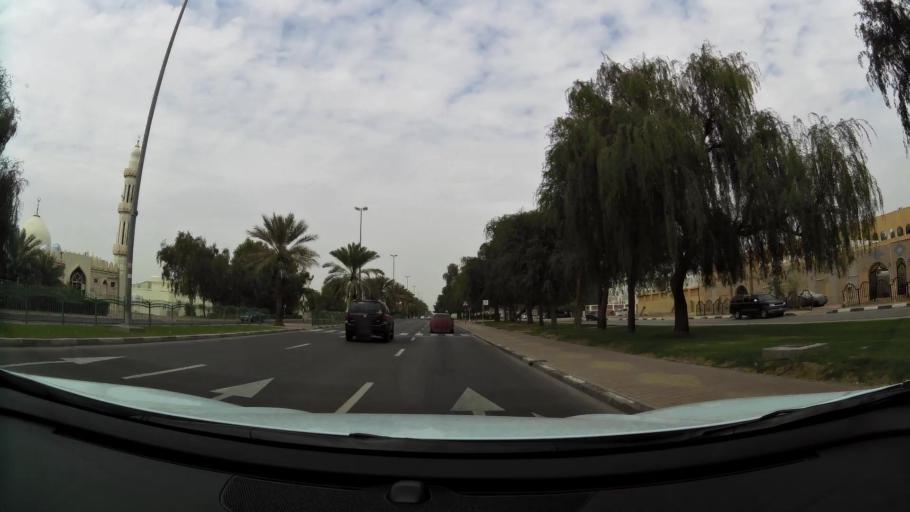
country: OM
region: Al Buraimi
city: Al Buraymi
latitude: 24.2171
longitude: 55.7862
